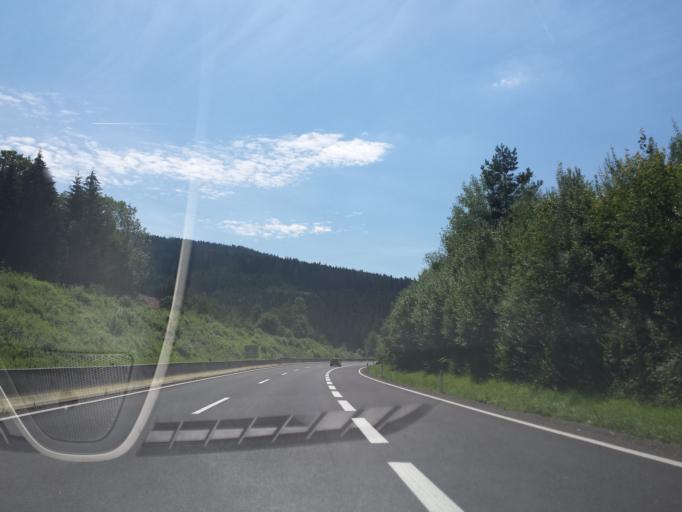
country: AT
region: Styria
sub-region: Politischer Bezirk Bruck-Muerzzuschlag
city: Mitterdorf im Muerztal
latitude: 47.5298
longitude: 15.5209
